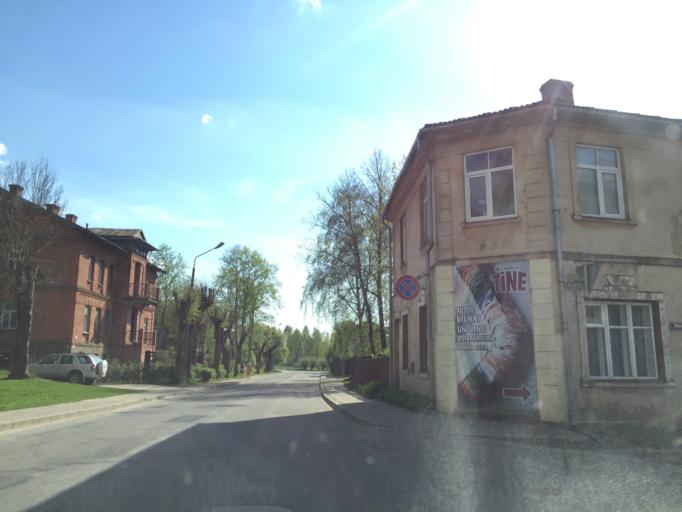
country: LV
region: Limbazu Rajons
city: Limbazi
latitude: 57.5114
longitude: 24.7070
